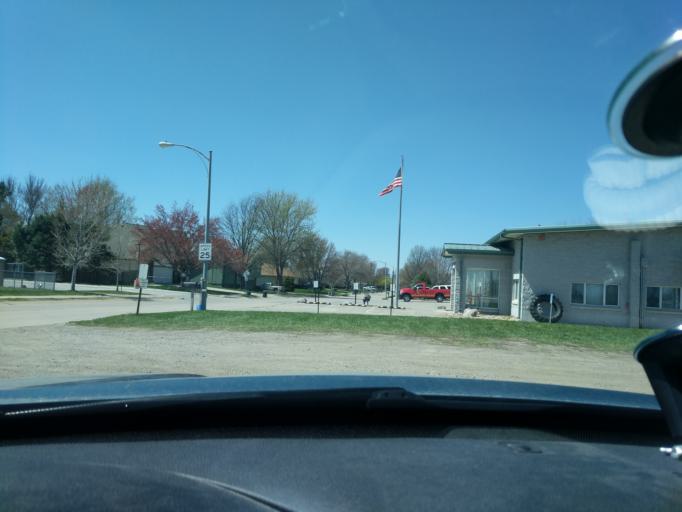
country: US
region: Nebraska
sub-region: Douglas County
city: Elkhorn
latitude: 41.2948
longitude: -96.2348
